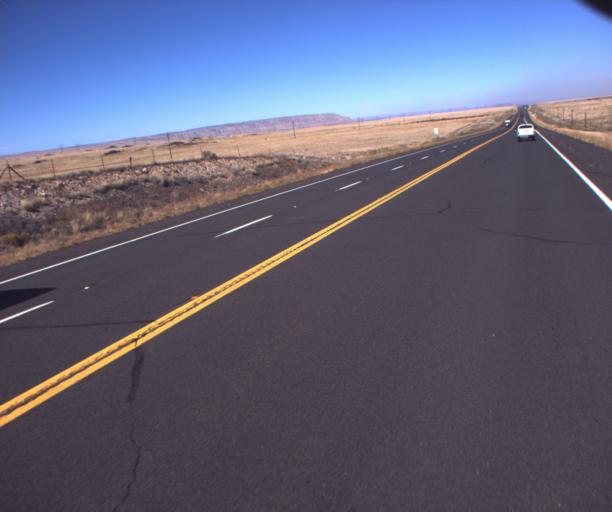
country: US
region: Arizona
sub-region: Coconino County
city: Flagstaff
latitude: 35.6344
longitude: -111.5193
